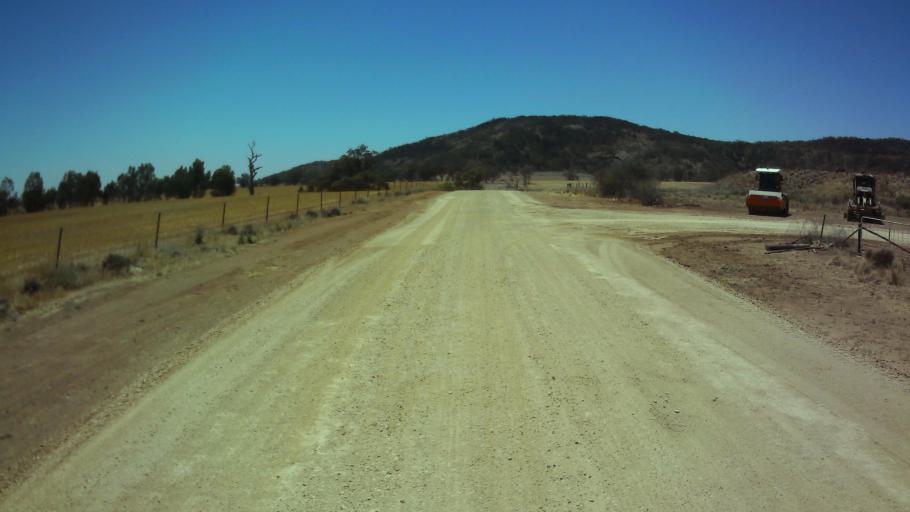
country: AU
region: New South Wales
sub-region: Weddin
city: Grenfell
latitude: -33.8562
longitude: 148.1076
